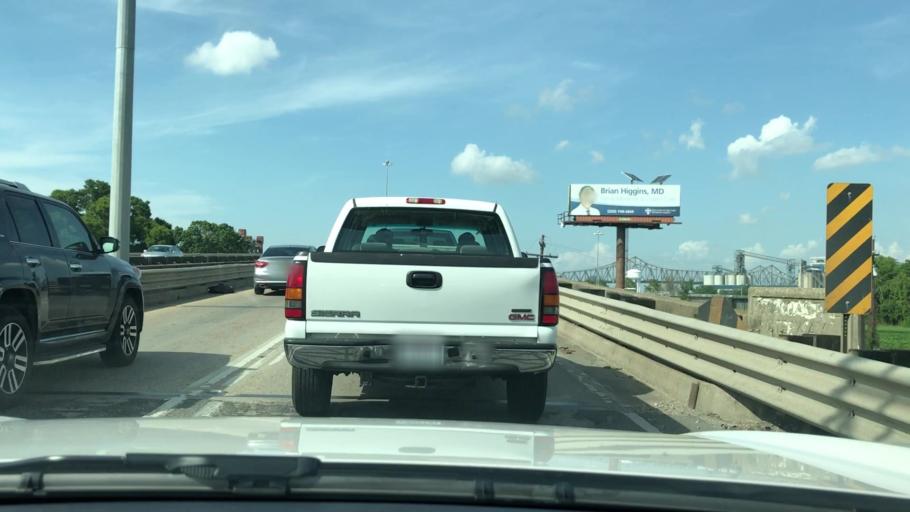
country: US
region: Louisiana
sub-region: West Baton Rouge Parish
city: Port Allen
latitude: 30.4292
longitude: -91.2131
